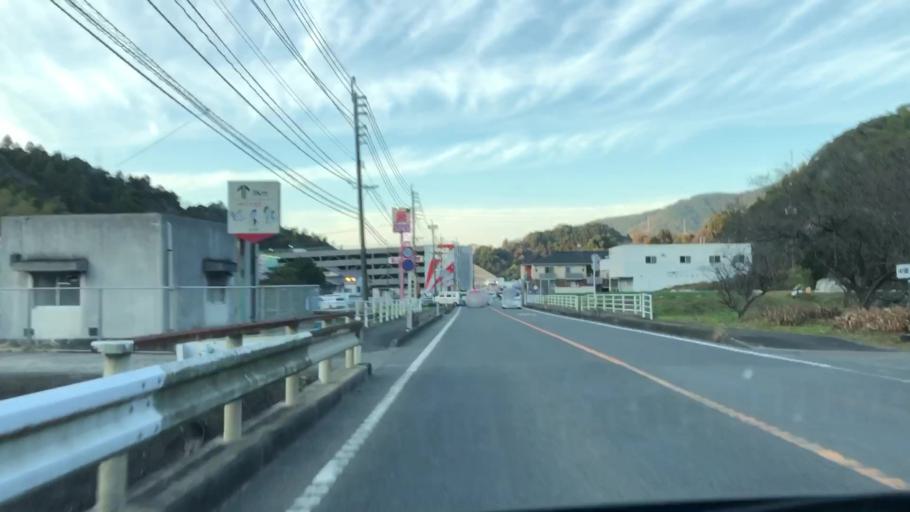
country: JP
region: Kumamoto
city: Minamata
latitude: 32.2208
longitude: 130.4382
